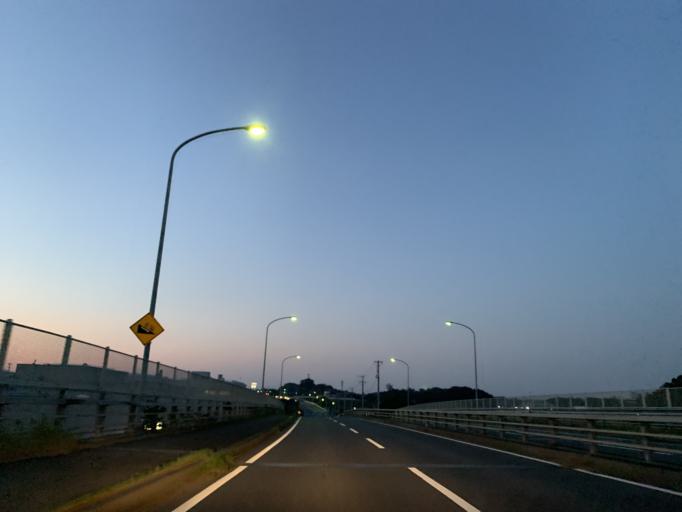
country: JP
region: Chiba
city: Nagareyama
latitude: 35.8717
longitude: 139.9080
